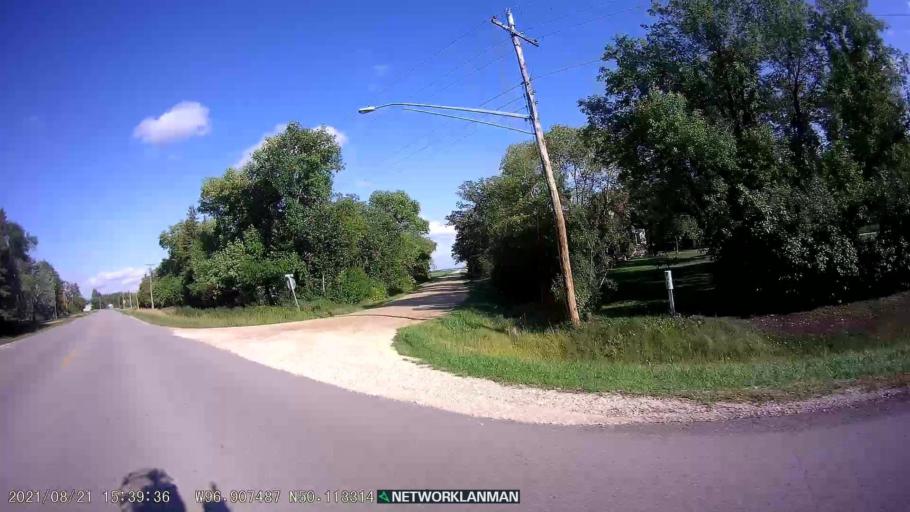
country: CA
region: Manitoba
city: Selkirk
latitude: 50.1135
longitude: -96.9068
